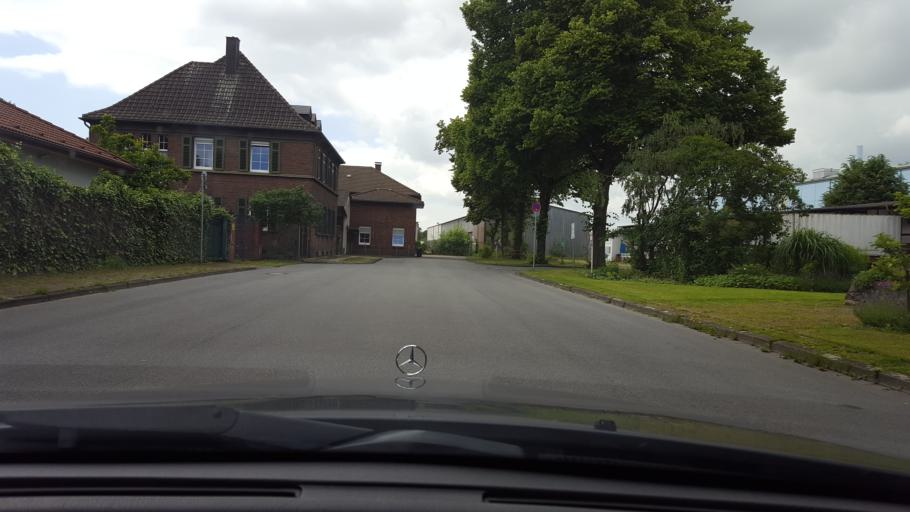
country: DE
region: North Rhine-Westphalia
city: Oer-Erkenschwick
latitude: 51.6235
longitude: 7.3211
